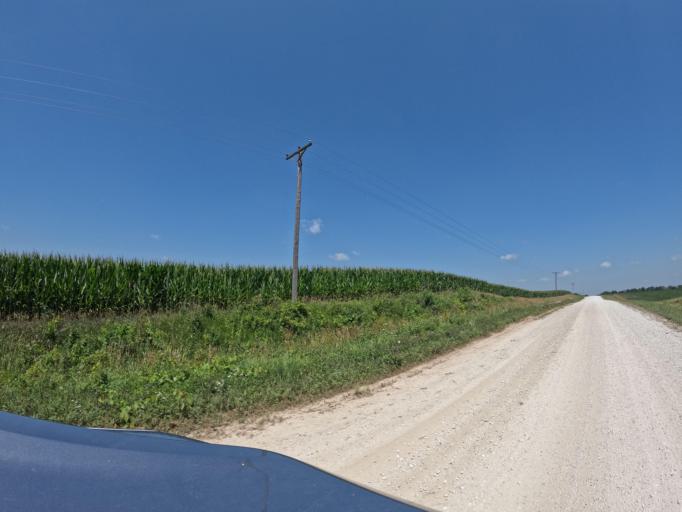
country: US
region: Iowa
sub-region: Keokuk County
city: Sigourney
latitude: 41.2758
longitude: -92.2381
